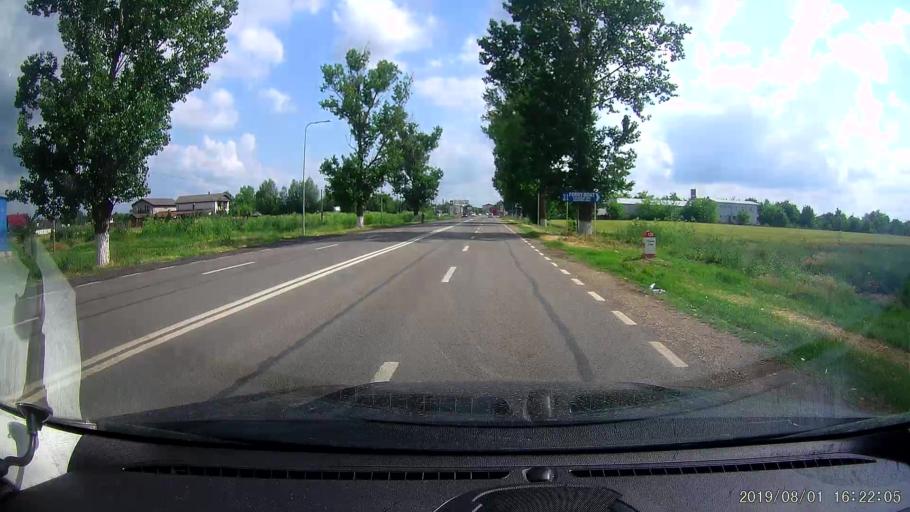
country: RO
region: Calarasi
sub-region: Municipiul Calarasi
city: Calarasi
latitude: 44.2079
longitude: 27.3383
